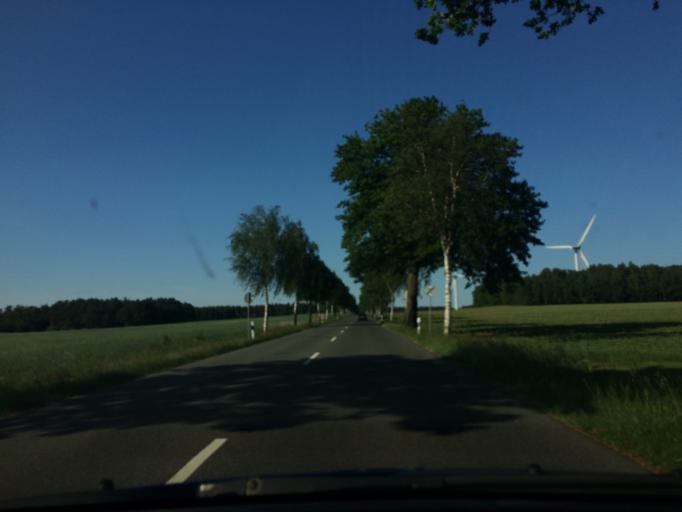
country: DE
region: Lower Saxony
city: Bispingen
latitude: 53.0379
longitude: 9.9300
